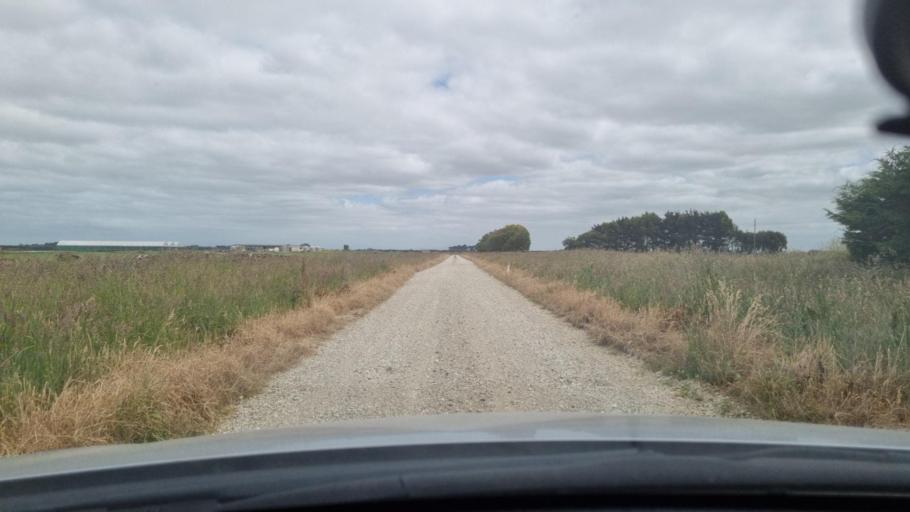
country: NZ
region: Southland
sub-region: Invercargill City
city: Invercargill
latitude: -46.4237
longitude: 168.3146
